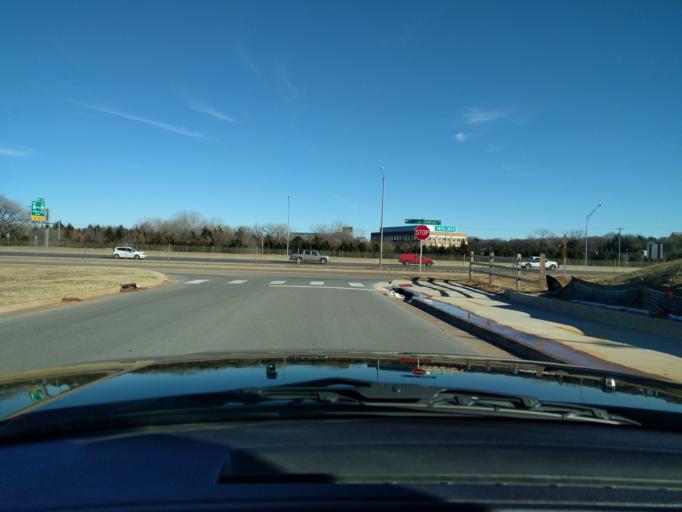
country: US
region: Oklahoma
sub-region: Oklahoma County
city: Edmond
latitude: 35.6448
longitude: -97.4257
